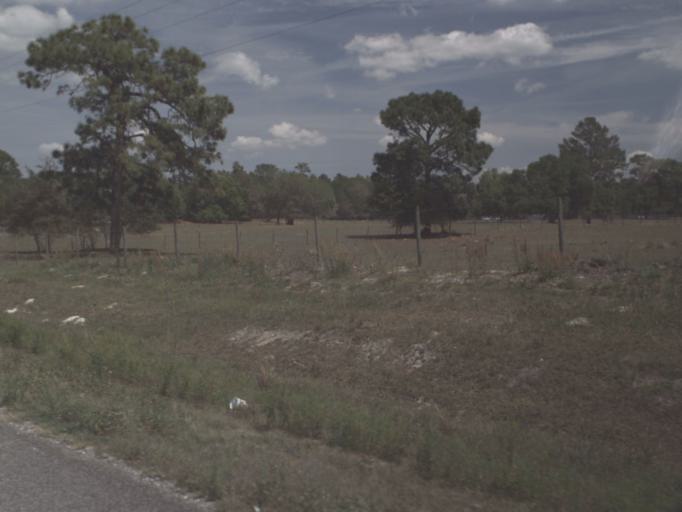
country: US
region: Florida
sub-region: Sumter County
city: Lake Panasoffkee
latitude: 28.7279
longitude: -82.0544
